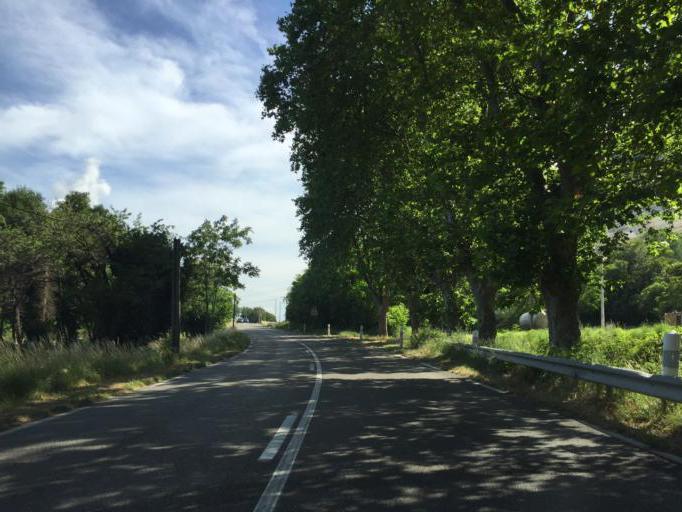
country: FR
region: Rhone-Alpes
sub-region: Departement de l'Ardeche
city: Cruas
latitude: 44.6430
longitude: 4.7515
